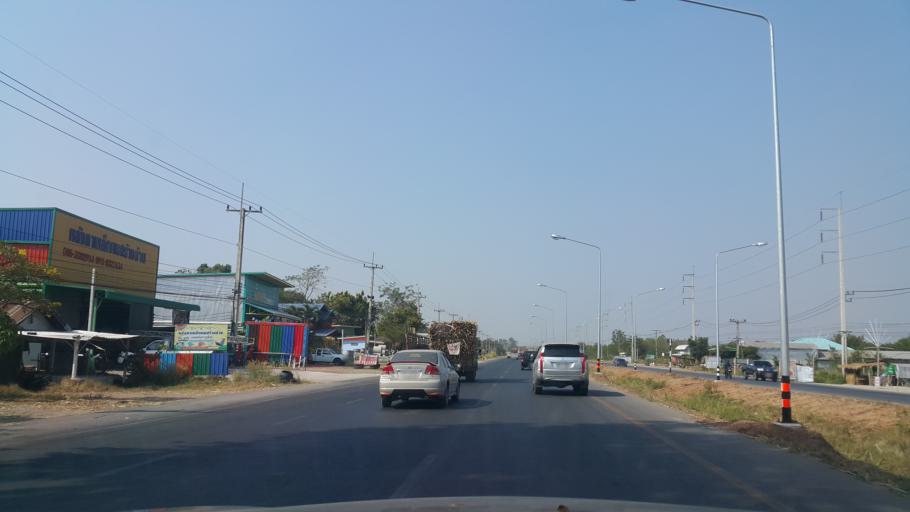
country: TH
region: Chaiyaphum
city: Phu Khiao
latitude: 16.4260
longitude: 102.1297
